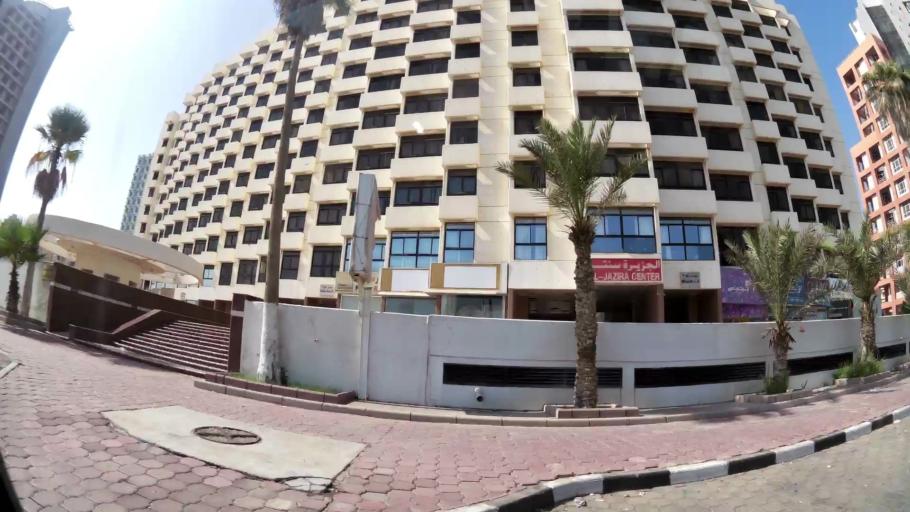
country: KW
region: Muhafazat Hawalli
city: As Salimiyah
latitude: 29.3343
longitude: 48.0933
